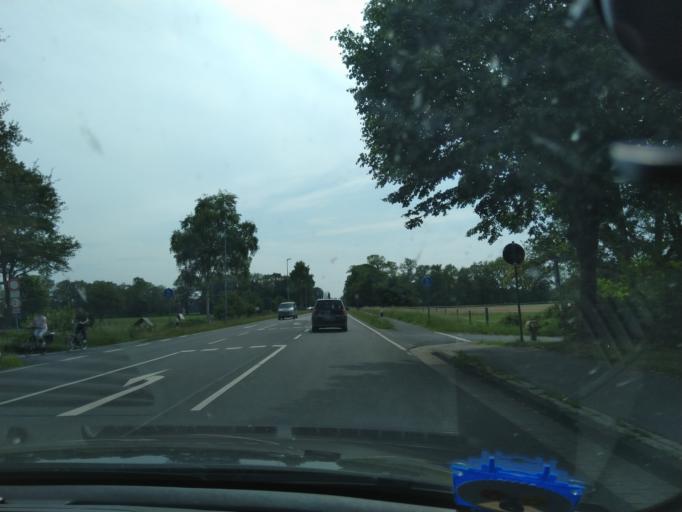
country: DE
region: Lower Saxony
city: Nordhorn
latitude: 52.4070
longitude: 7.0391
